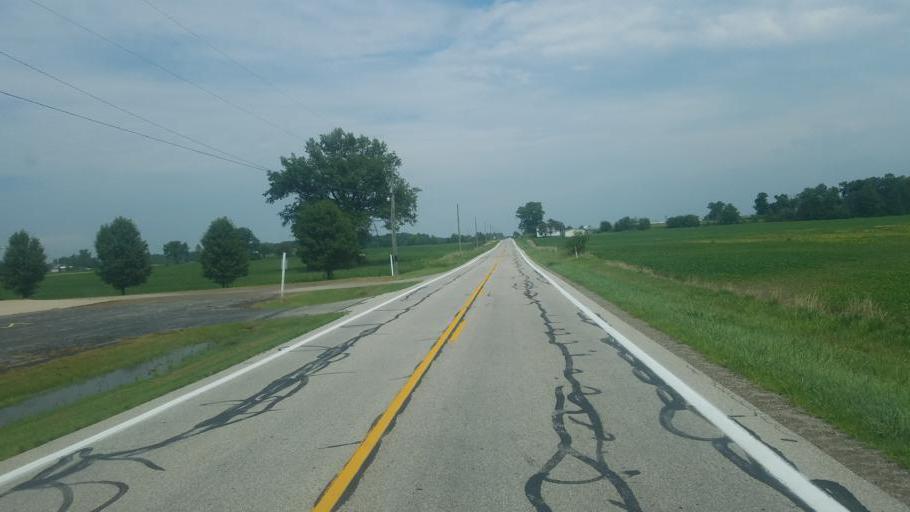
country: US
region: Ohio
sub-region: Union County
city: Marysville
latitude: 40.3468
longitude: -83.3851
